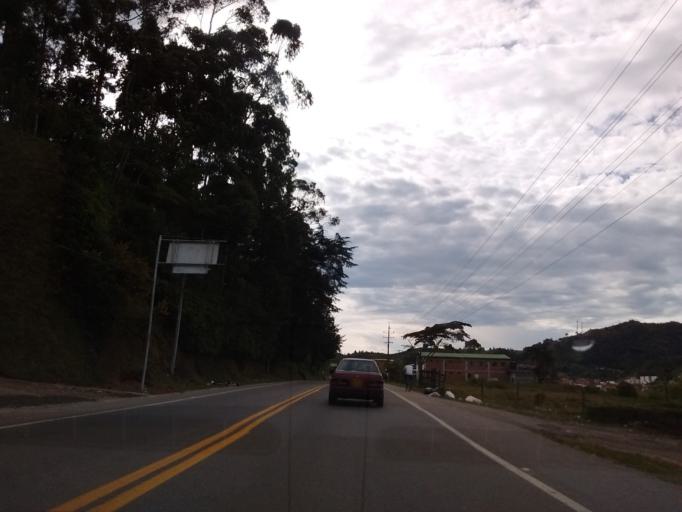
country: CO
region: Antioquia
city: Santuario
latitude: 6.1326
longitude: -75.2606
